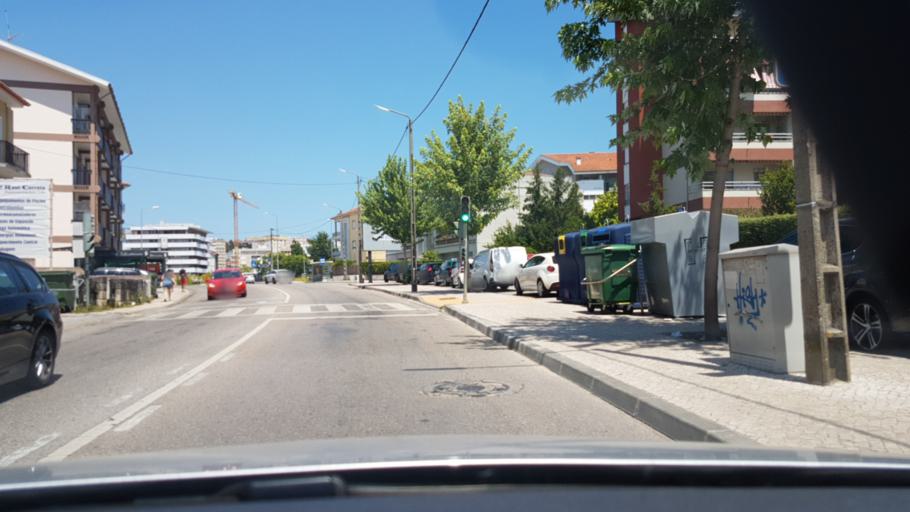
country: PT
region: Coimbra
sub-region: Coimbra
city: Coimbra
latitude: 40.1983
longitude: -8.4027
